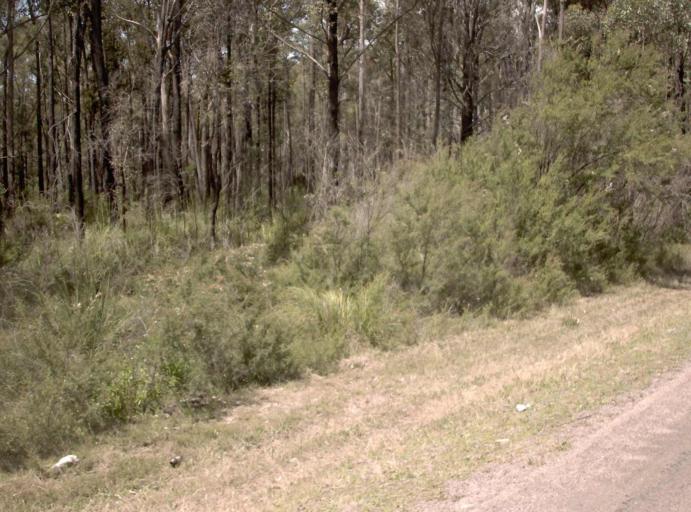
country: AU
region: New South Wales
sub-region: Bombala
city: Bombala
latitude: -37.5664
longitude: 149.1073
